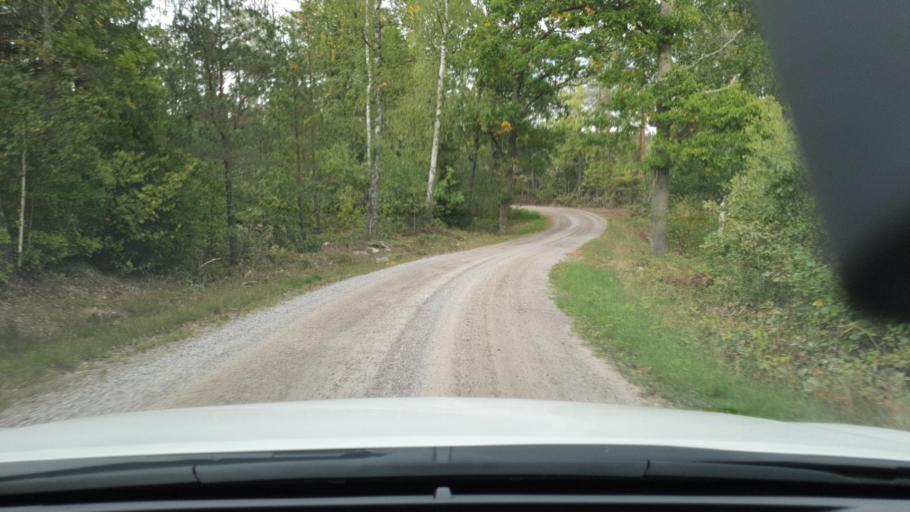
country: SE
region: Kalmar
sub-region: Vasterviks Kommun
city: Vaestervik
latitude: 57.7333
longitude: 16.4848
